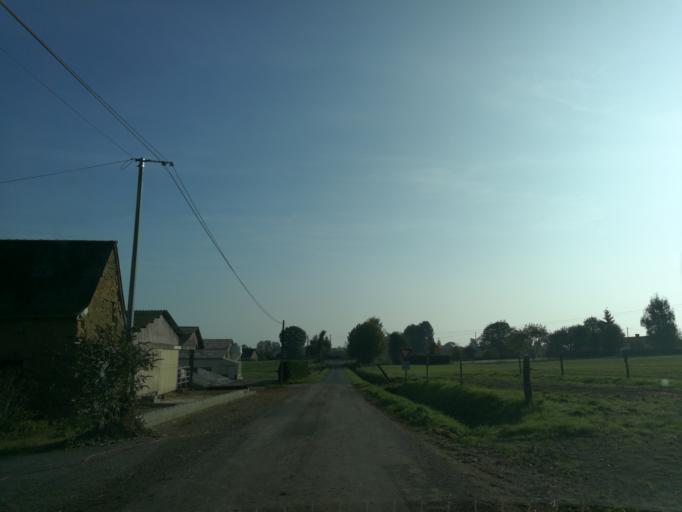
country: FR
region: Brittany
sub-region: Departement d'Ille-et-Vilaine
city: Breteil
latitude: 48.1555
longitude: -1.8969
